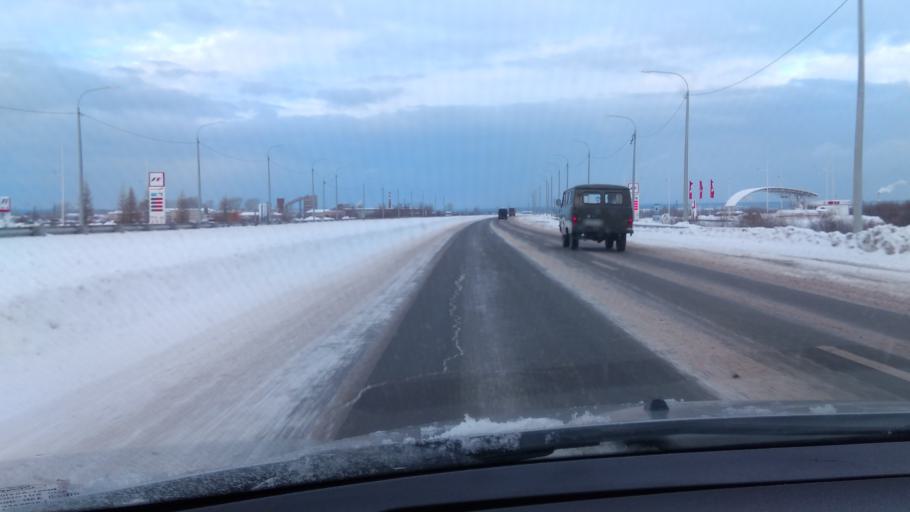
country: RU
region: Sverdlovsk
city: Tsementnyy
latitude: 57.4664
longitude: 60.1848
